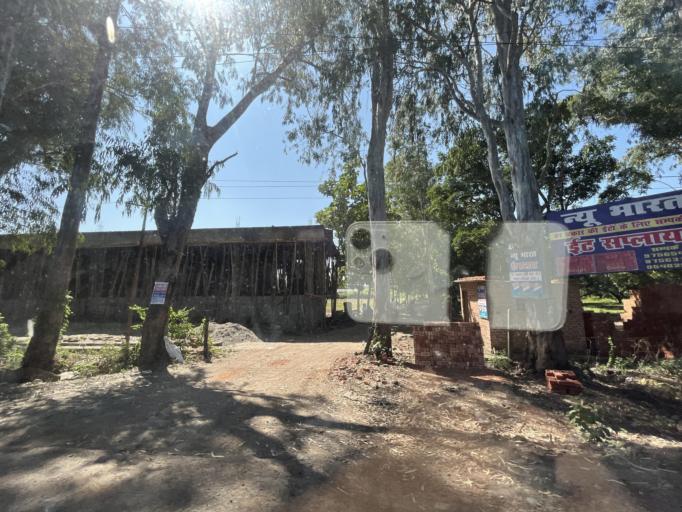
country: IN
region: Uttarakhand
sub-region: Naini Tal
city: Haldwani
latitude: 29.2127
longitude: 79.4574
